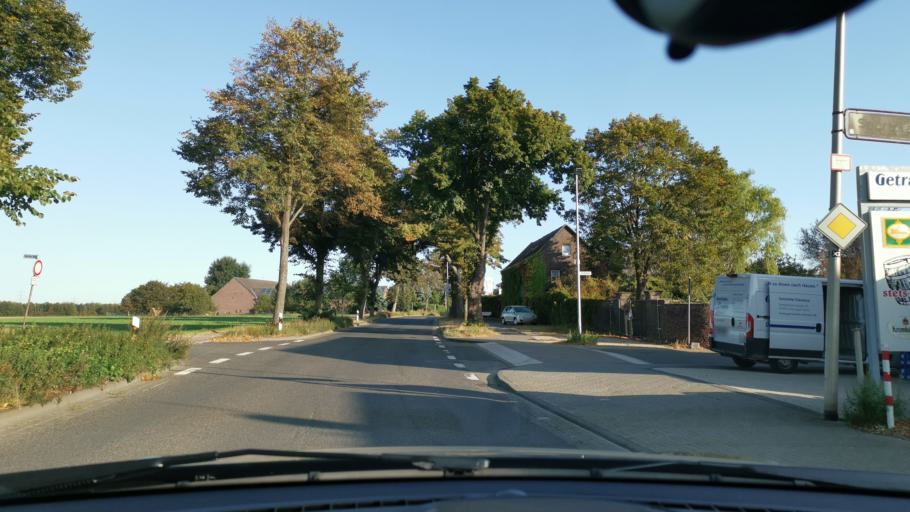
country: DE
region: North Rhine-Westphalia
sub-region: Regierungsbezirk Dusseldorf
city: Rommerskirchen
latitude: 51.1035
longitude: 6.7173
